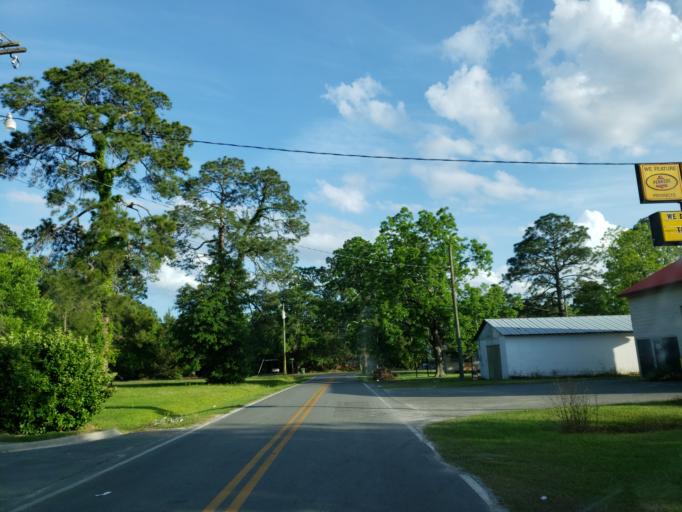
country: US
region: Georgia
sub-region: Cook County
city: Adel
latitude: 31.1344
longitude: -83.4314
